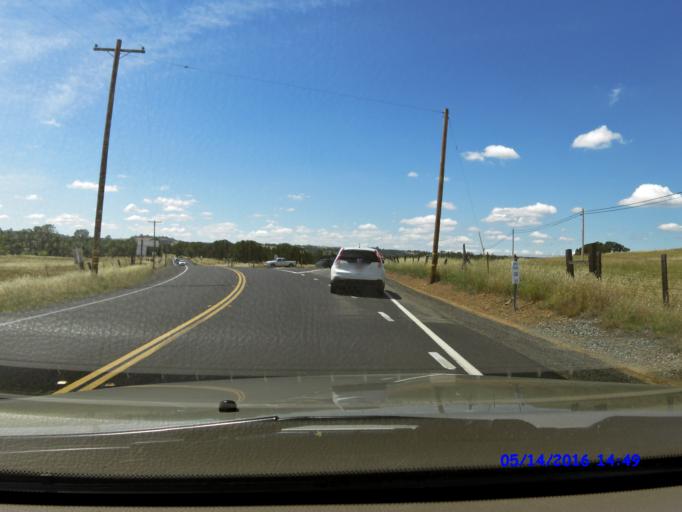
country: US
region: California
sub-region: Tuolumne County
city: Jamestown
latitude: 37.8743
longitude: -120.4339
